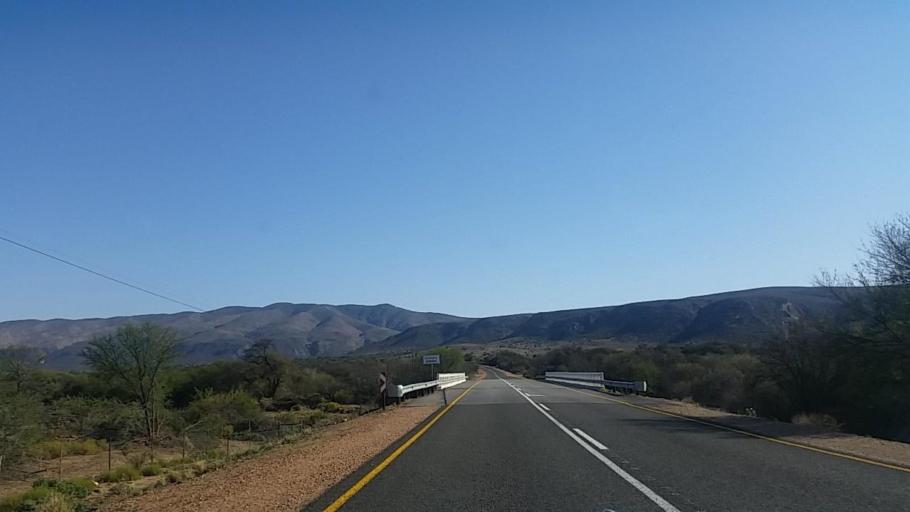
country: ZA
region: Eastern Cape
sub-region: Cacadu District Municipality
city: Willowmore
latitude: -33.4555
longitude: 23.3121
